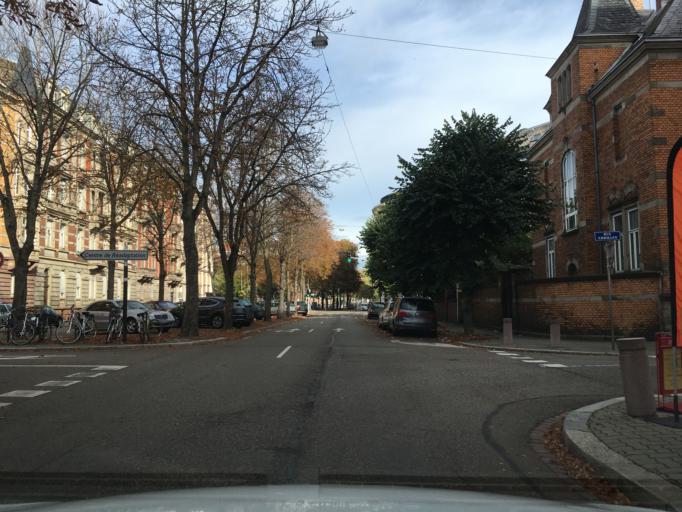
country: FR
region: Alsace
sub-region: Departement du Bas-Rhin
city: Strasbourg
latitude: 48.5920
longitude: 7.7548
